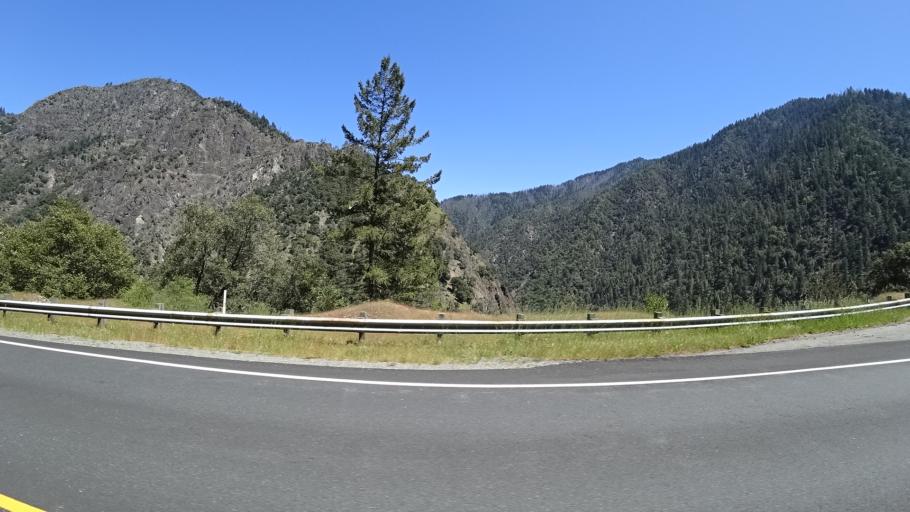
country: US
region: California
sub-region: Humboldt County
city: Willow Creek
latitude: 40.8468
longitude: -123.4833
